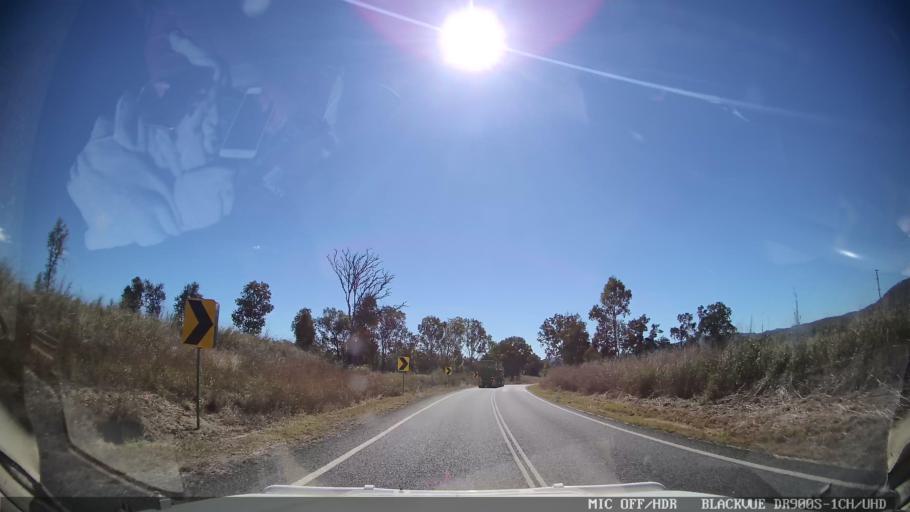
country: AU
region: Queensland
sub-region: Gladstone
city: Toolooa
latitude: -24.2770
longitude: 151.2765
